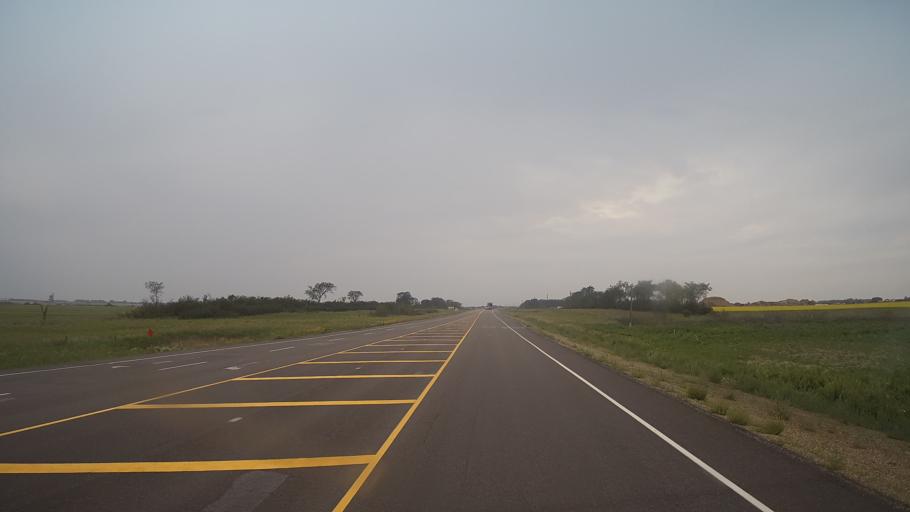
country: CA
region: Saskatchewan
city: Dalmeny
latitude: 52.1293
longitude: -106.8626
